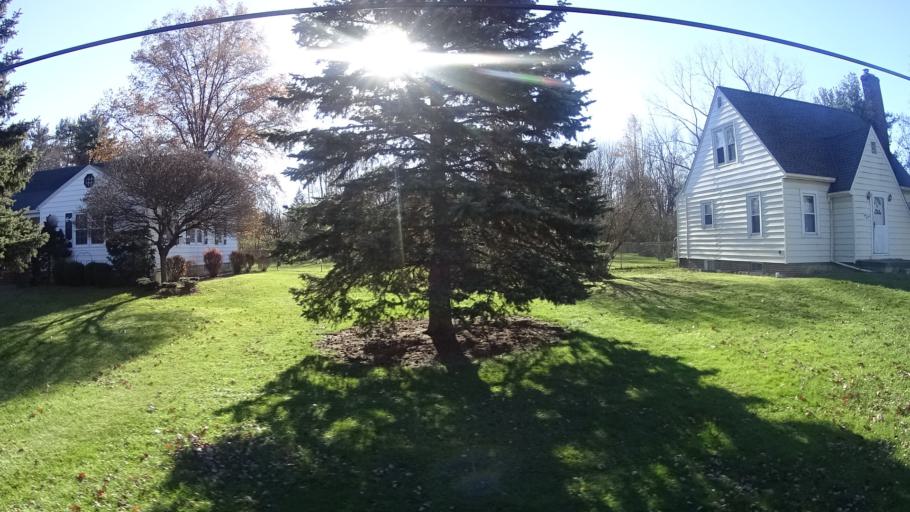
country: US
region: Ohio
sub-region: Lorain County
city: Sheffield
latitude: 41.4089
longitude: -82.1112
